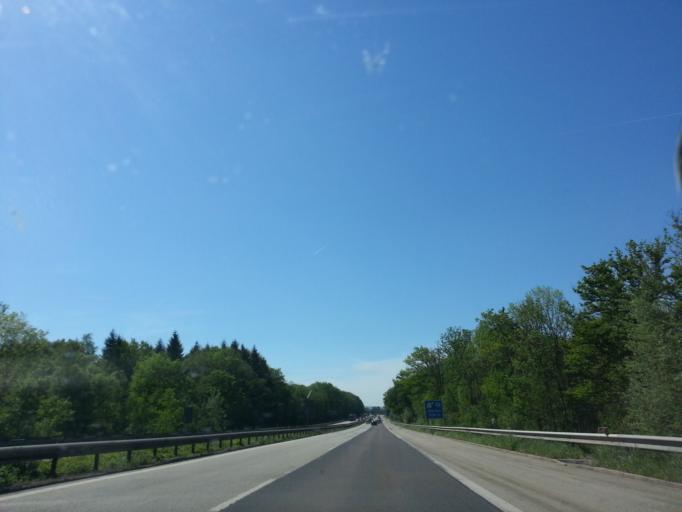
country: DE
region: Bavaria
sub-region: Upper Bavaria
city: Ubersee
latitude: 47.8342
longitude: 12.5051
